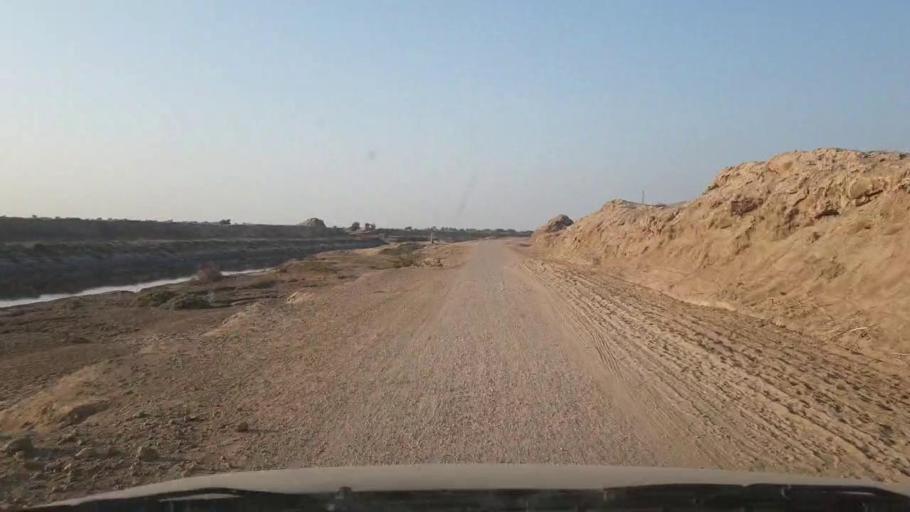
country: PK
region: Sindh
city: Samaro
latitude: 25.2923
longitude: 69.3323
